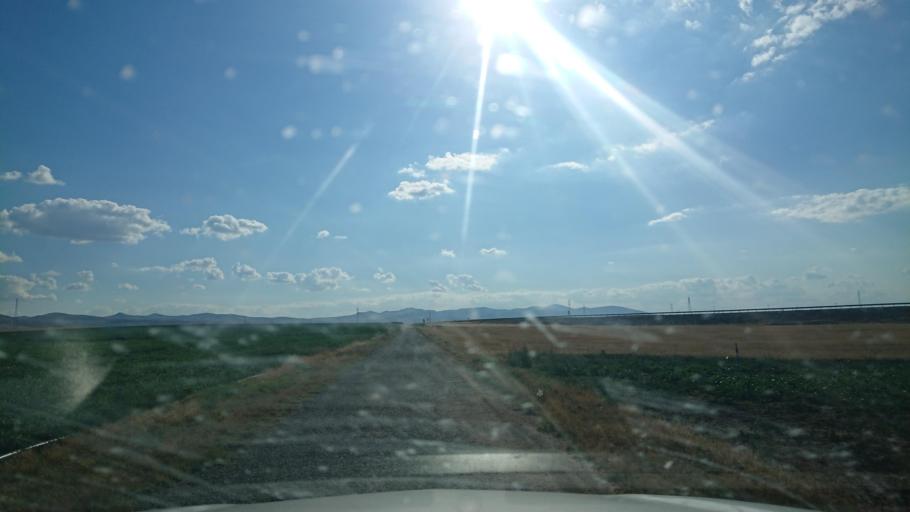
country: TR
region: Aksaray
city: Sariyahsi
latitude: 39.0201
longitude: 33.8844
